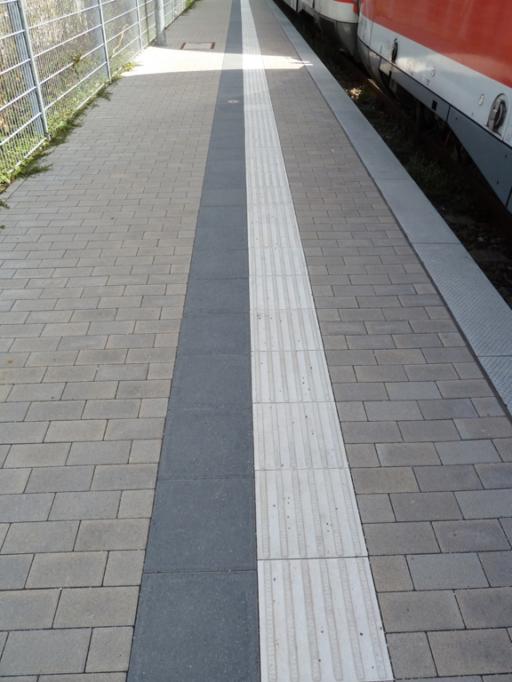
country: DE
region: Baden-Wuerttemberg
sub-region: Tuebingen Region
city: Dornstadt
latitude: 48.4150
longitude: 9.9188
